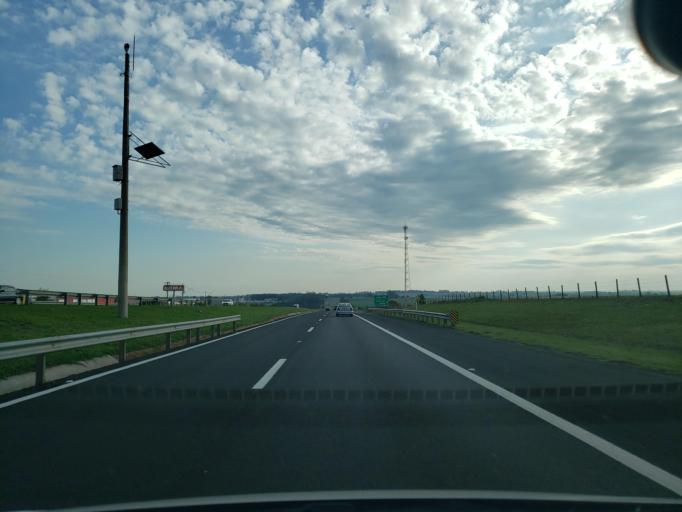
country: BR
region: Sao Paulo
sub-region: Guararapes
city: Guararapes
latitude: -21.2066
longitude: -50.6412
